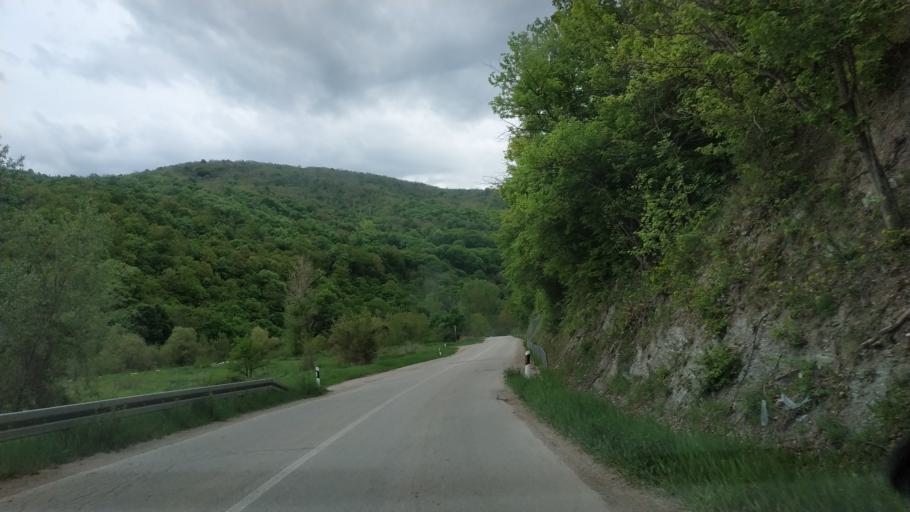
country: RS
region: Central Serbia
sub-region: Nisavski Okrug
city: Aleksinac
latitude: 43.6299
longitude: 21.7153
